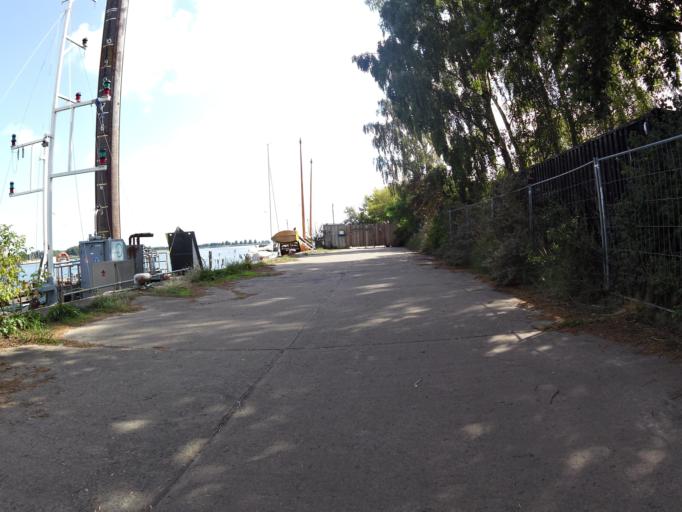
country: DE
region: Mecklenburg-Vorpommern
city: Kroslin
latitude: 54.1349
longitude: 13.7635
